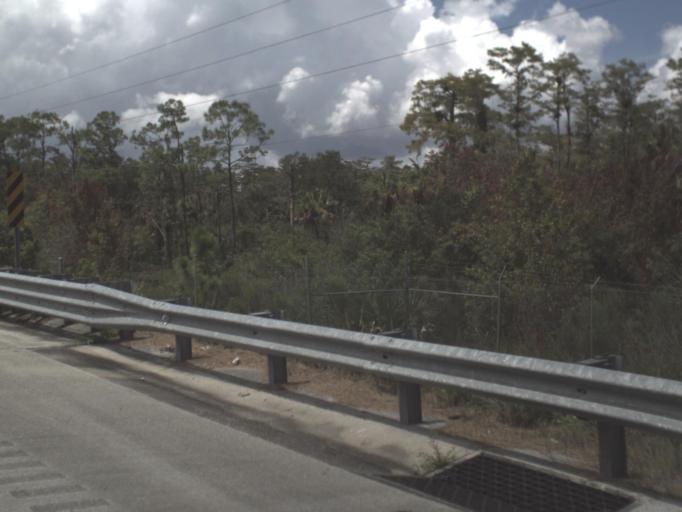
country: US
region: Florida
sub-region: Collier County
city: Immokalee
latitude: 26.1556
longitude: -81.2789
